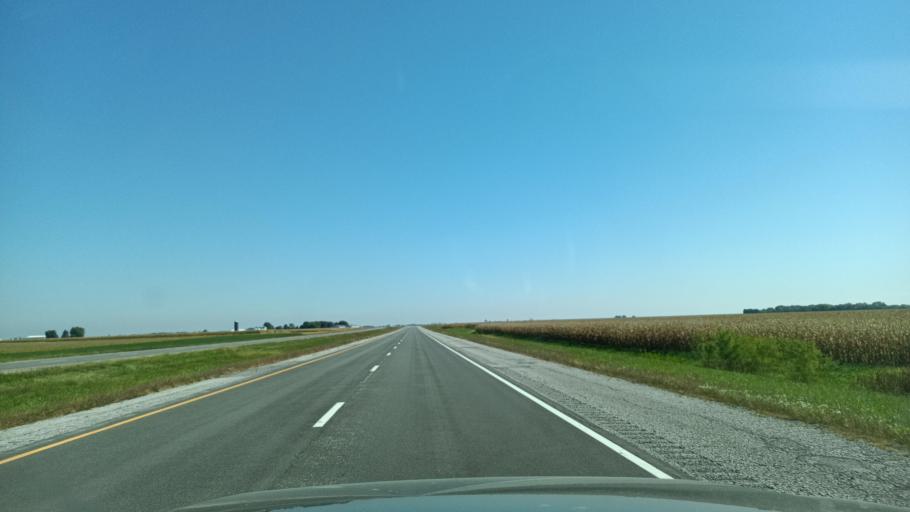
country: US
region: Illinois
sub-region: Adams County
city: Camp Point
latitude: 40.2085
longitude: -91.1349
